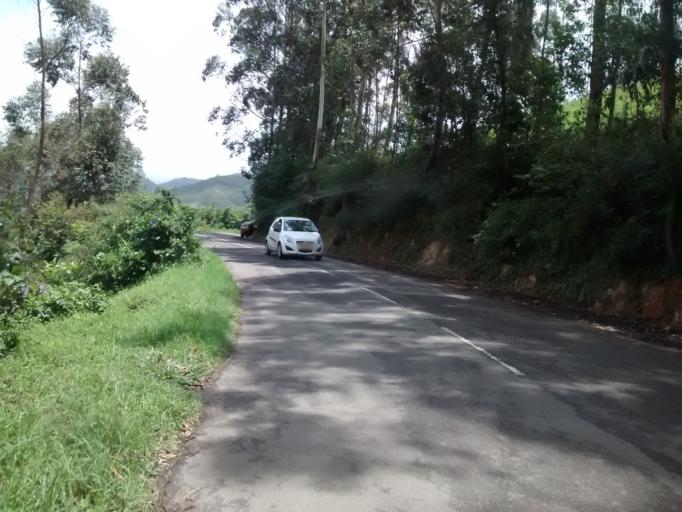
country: IN
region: Kerala
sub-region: Idukki
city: Munnar
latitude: 10.1117
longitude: 77.1334
